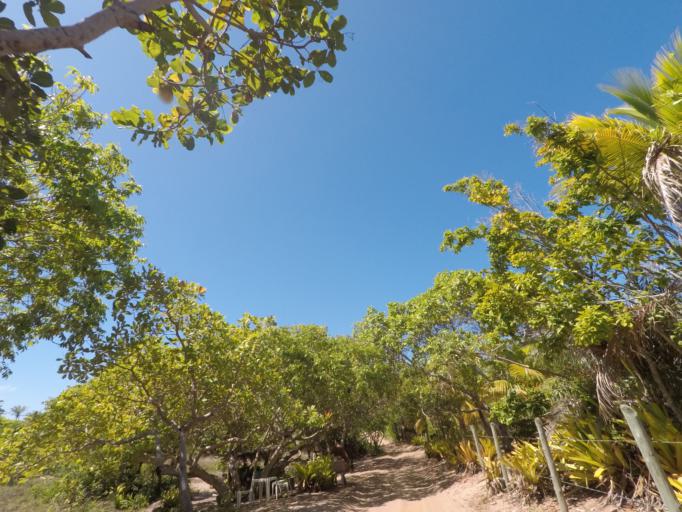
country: BR
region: Bahia
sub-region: Marau
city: Marau
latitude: -13.9558
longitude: -38.9346
